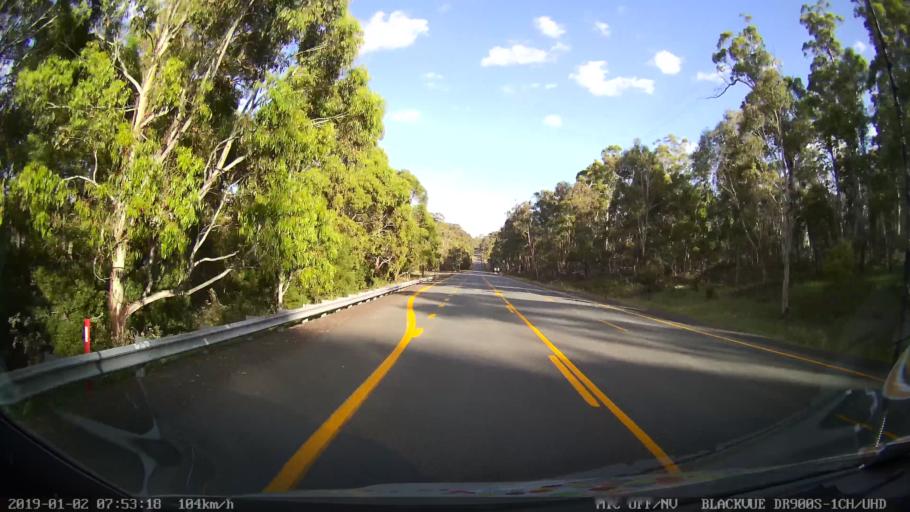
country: AU
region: New South Wales
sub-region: Tumut Shire
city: Tumut
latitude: -35.7070
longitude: 148.5082
